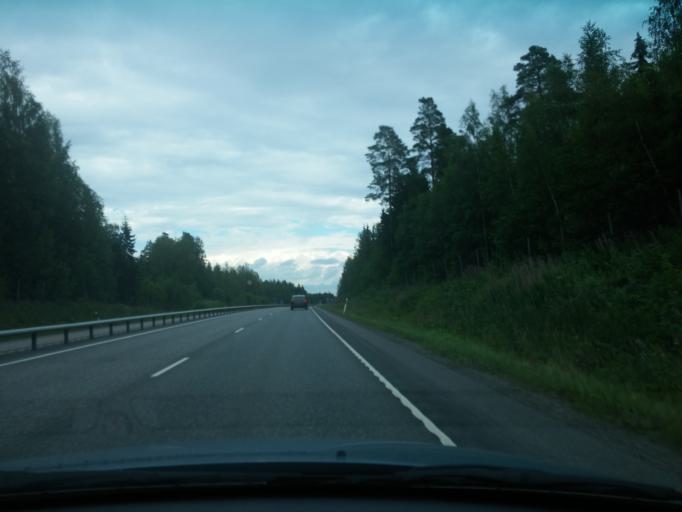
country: FI
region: Haeme
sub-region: Riihimaeki
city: Loppi
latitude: 60.7224
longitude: 24.5032
